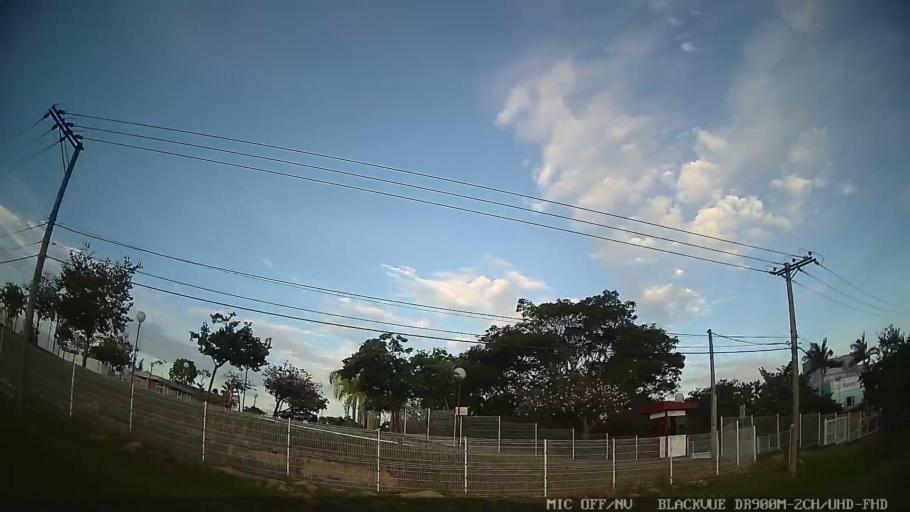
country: BR
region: Sao Paulo
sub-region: Salto
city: Salto
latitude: -23.1801
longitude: -47.2767
